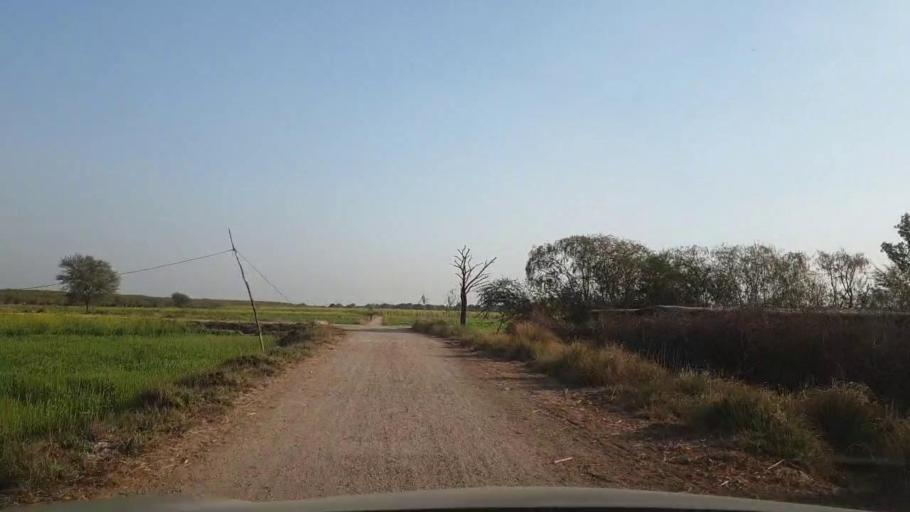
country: PK
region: Sindh
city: Tando Allahyar
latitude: 25.5869
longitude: 68.6708
